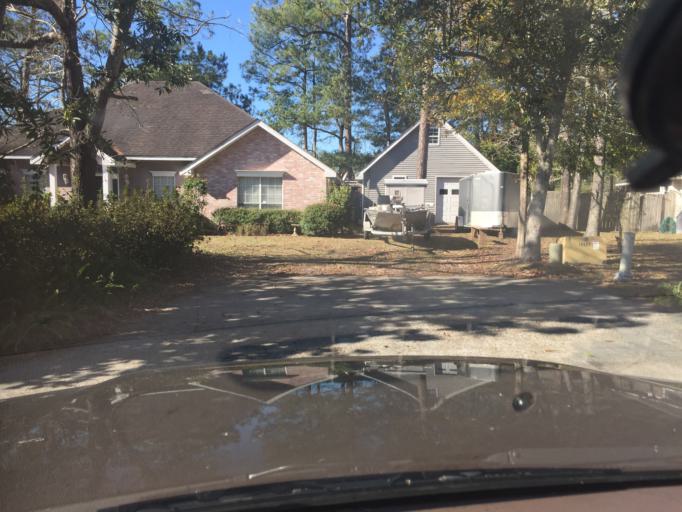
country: US
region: Louisiana
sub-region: Saint Tammany Parish
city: Slidell
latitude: 30.3032
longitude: -89.7373
